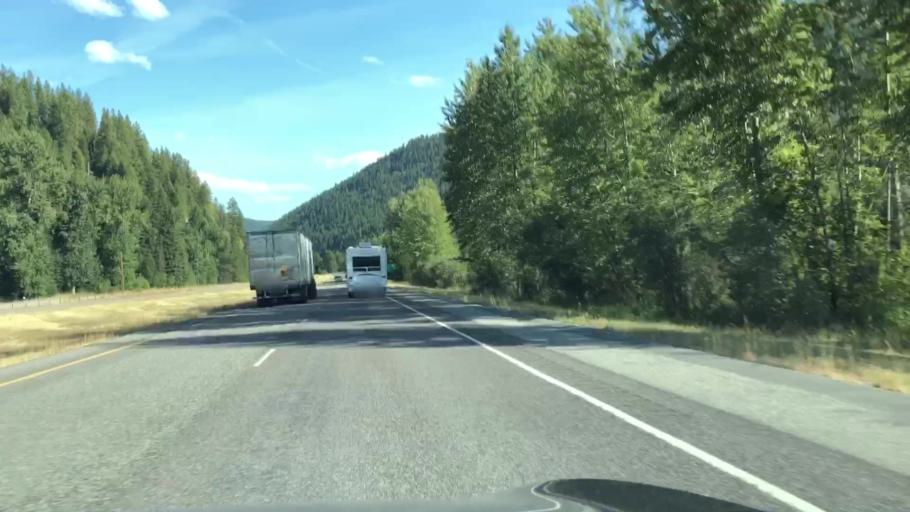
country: US
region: Montana
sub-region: Sanders County
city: Thompson Falls
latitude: 47.3629
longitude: -115.3238
